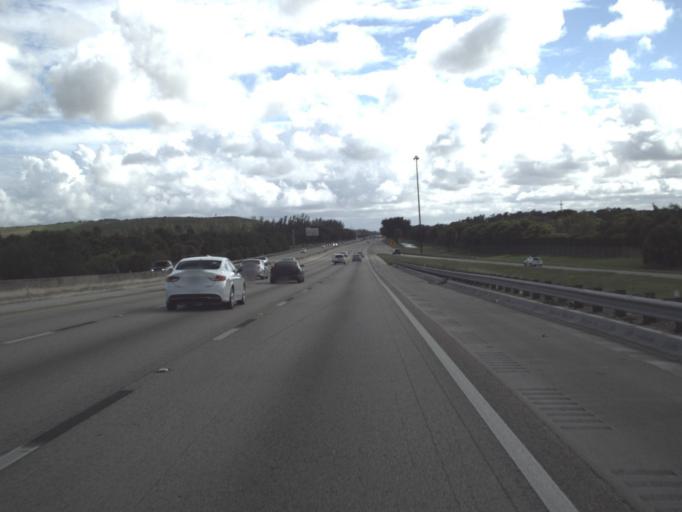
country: US
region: Florida
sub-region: Palm Beach County
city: Boca Pointe
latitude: 26.3033
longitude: -80.1696
